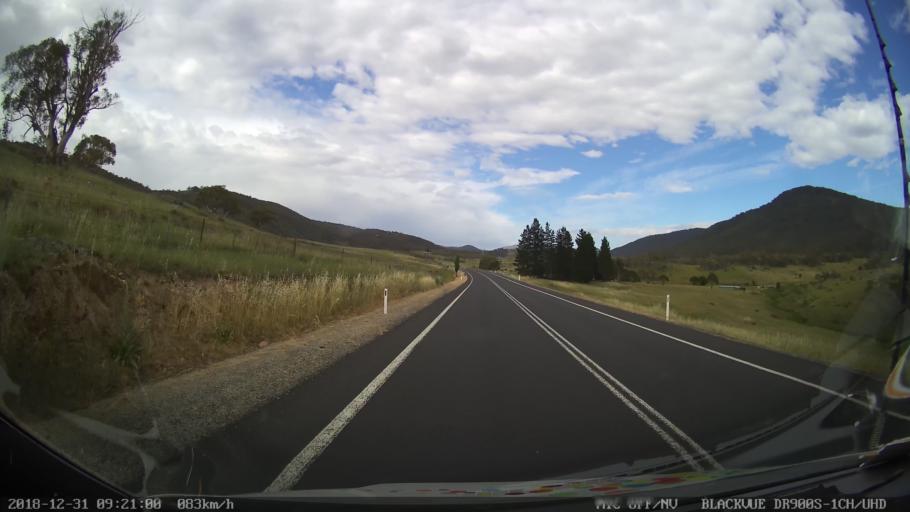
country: AU
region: New South Wales
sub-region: Snowy River
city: Jindabyne
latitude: -36.4255
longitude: 148.5672
